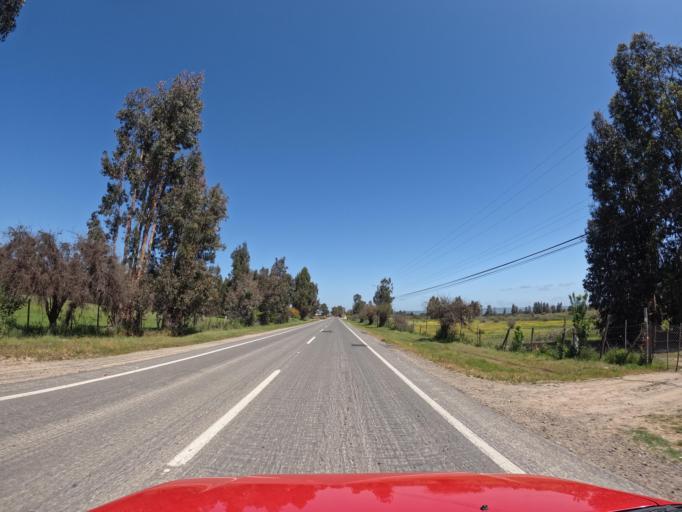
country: CL
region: O'Higgins
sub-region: Provincia de Colchagua
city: Santa Cruz
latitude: -34.7323
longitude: -71.6826
